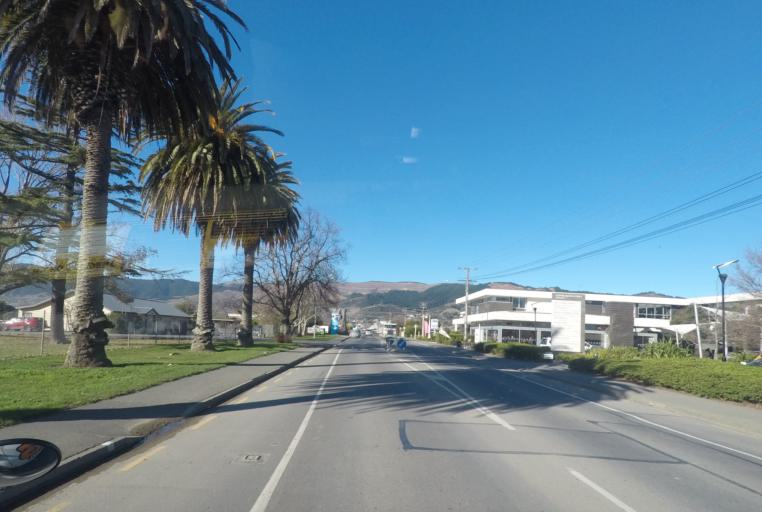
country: NZ
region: Tasman
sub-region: Tasman District
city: Richmond
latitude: -41.3343
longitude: 173.1794
